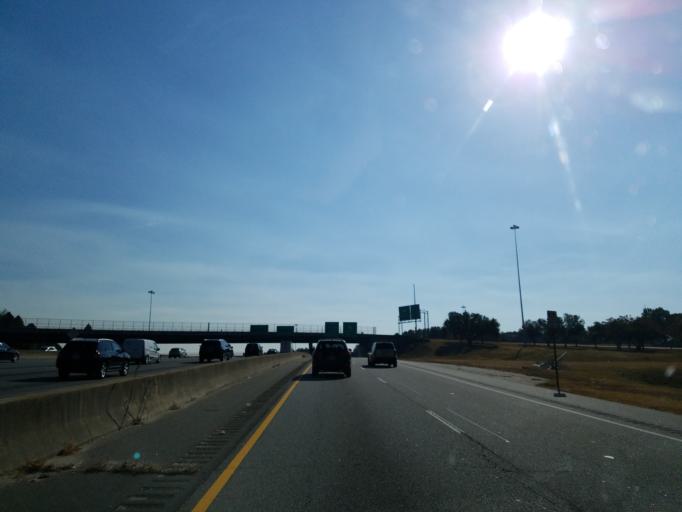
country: US
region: Georgia
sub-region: Fulton County
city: Hapeville
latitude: 33.6986
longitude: -84.4049
